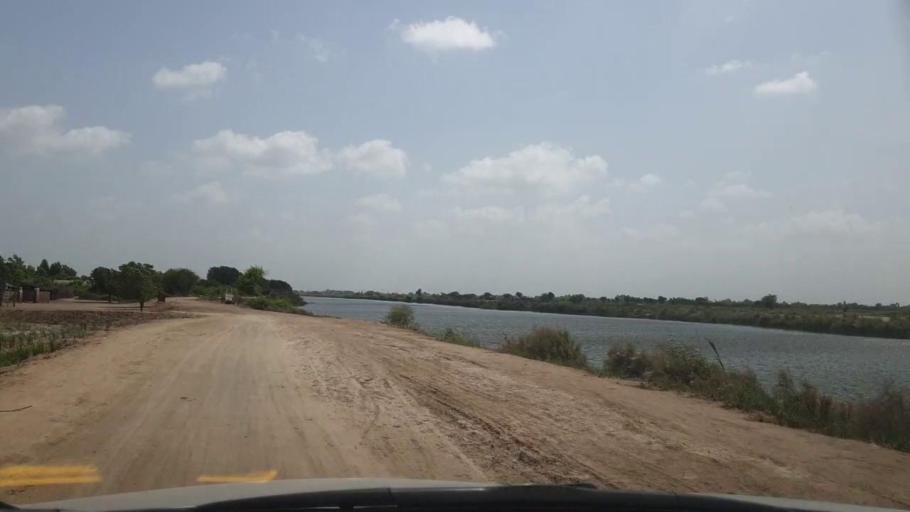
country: PK
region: Sindh
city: Talhar
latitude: 24.8741
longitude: 68.9138
